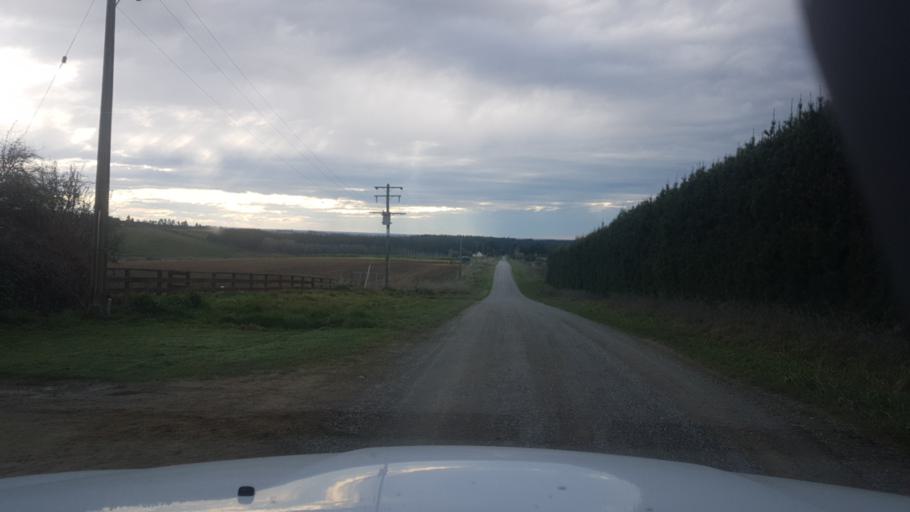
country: NZ
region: Canterbury
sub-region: Timaru District
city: Pleasant Point
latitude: -44.3375
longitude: 171.1484
